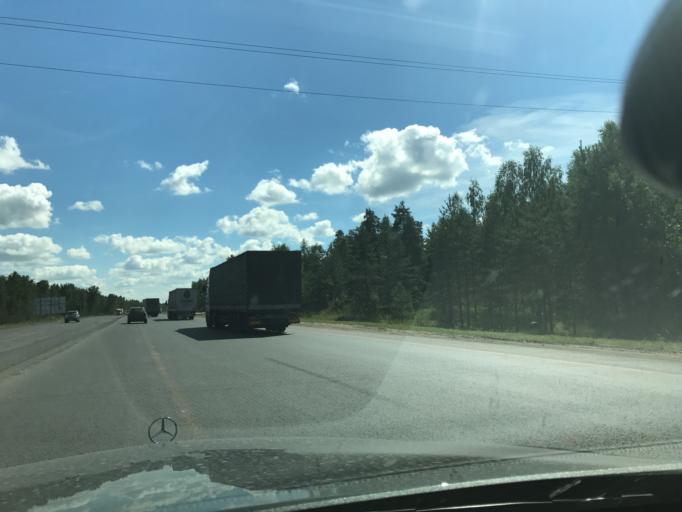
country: RU
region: Nizjnij Novgorod
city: Gorbatovka
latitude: 56.2972
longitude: 43.6922
